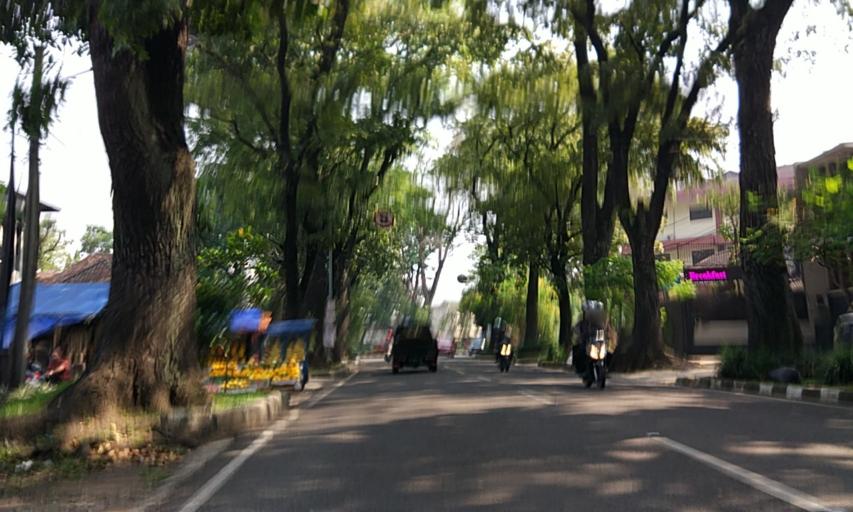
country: ID
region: West Java
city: Bandung
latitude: -6.9018
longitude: 107.5993
